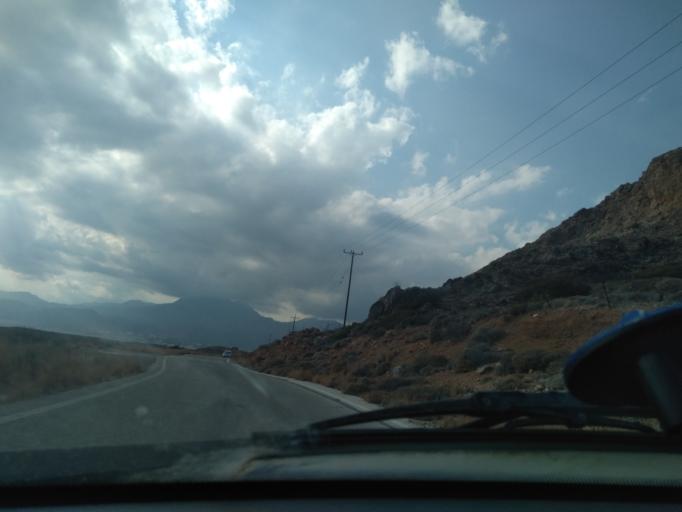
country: GR
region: Crete
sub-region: Nomos Lasithiou
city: Makry-Gialos
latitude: 35.0201
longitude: 26.0205
